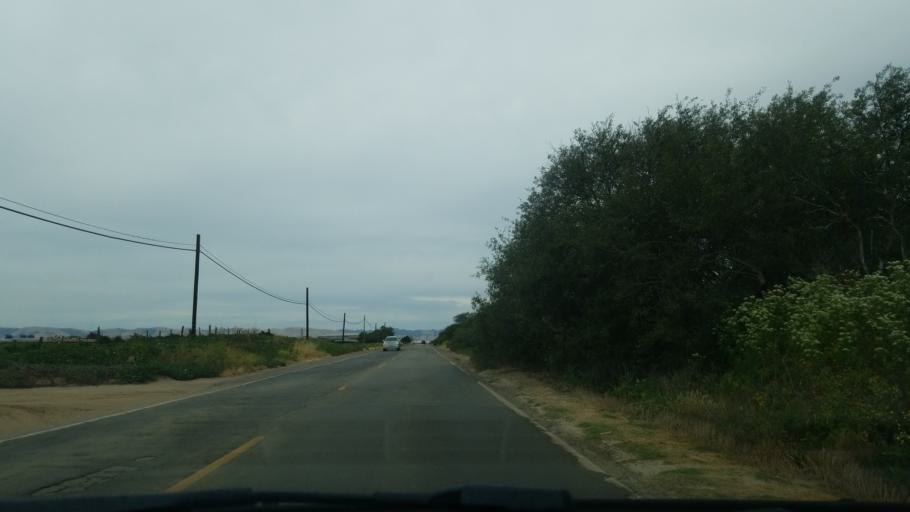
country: US
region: California
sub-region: Santa Barbara County
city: Santa Maria
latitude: 34.9148
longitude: -120.4832
